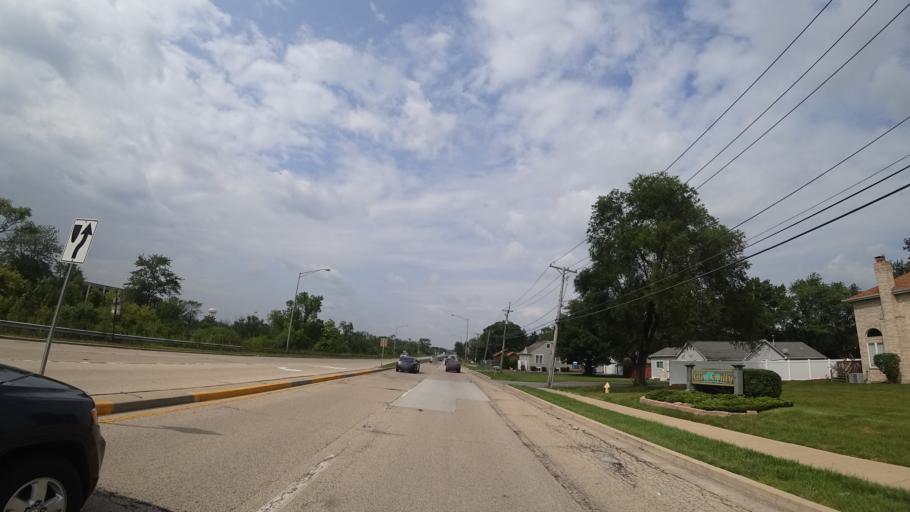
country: US
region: Illinois
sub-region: Cook County
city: Tinley Park
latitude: 41.5604
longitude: -87.7925
